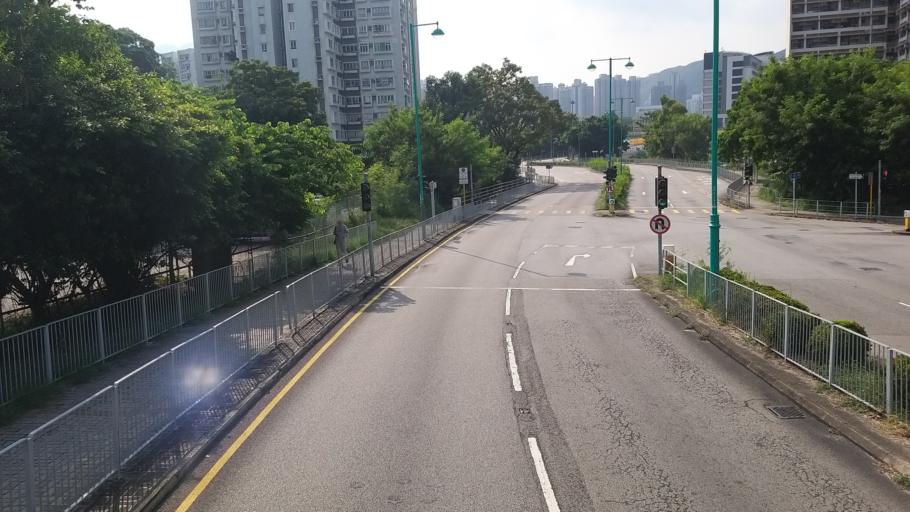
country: HK
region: Tuen Mun
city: Tuen Mun
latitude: 22.4087
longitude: 113.9812
